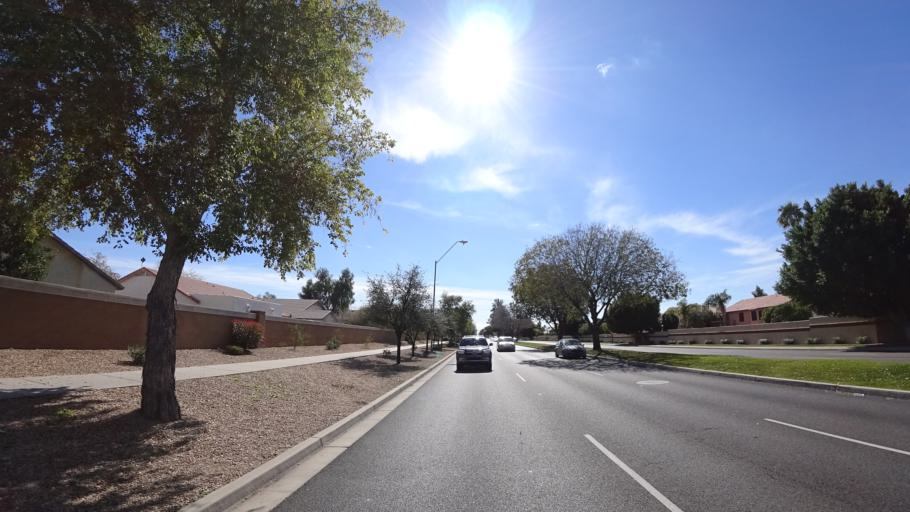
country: US
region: Arizona
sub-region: Maricopa County
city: Peoria
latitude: 33.6623
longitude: -112.2029
